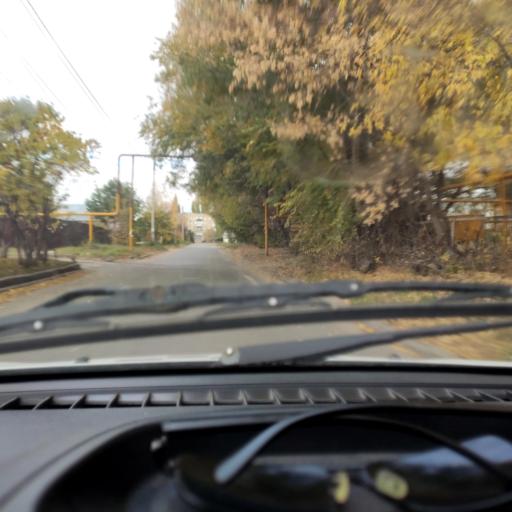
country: RU
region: Samara
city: Tol'yatti
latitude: 53.5301
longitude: 49.4290
